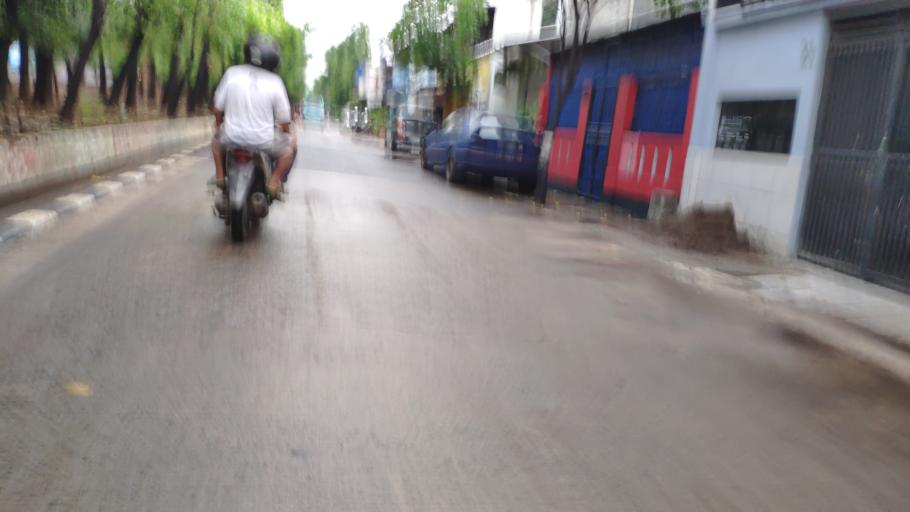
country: ID
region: Jakarta Raya
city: Jakarta
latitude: -6.2116
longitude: 106.8736
